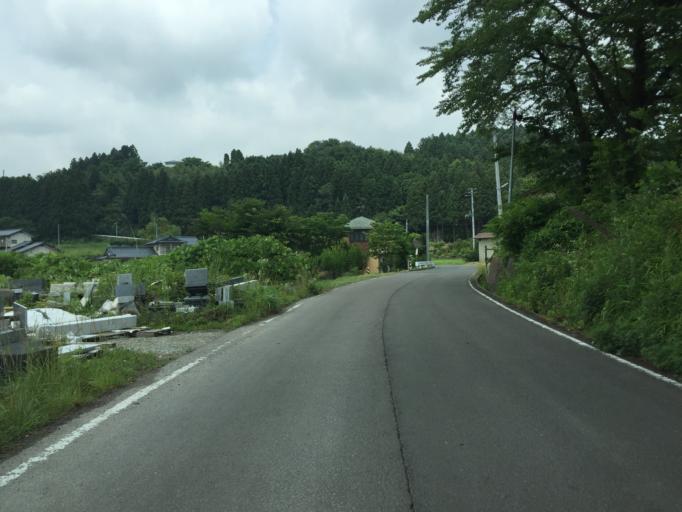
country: JP
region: Fukushima
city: Fukushima-shi
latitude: 37.7742
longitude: 140.3716
